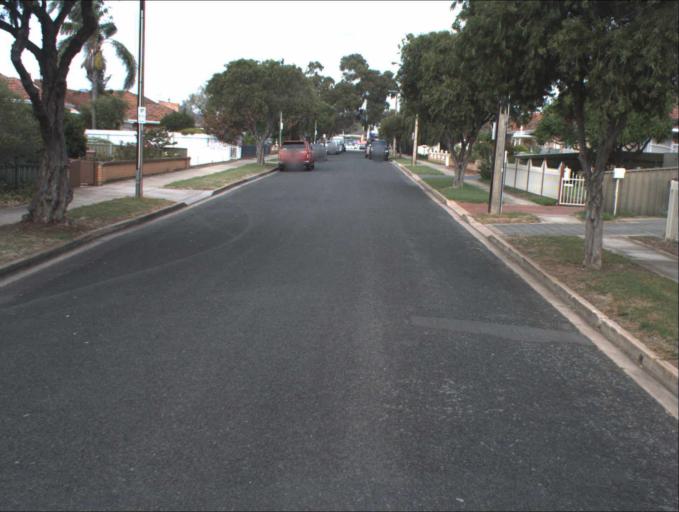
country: AU
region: South Australia
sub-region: Port Adelaide Enfield
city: Blair Athol
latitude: -34.8646
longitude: 138.5995
